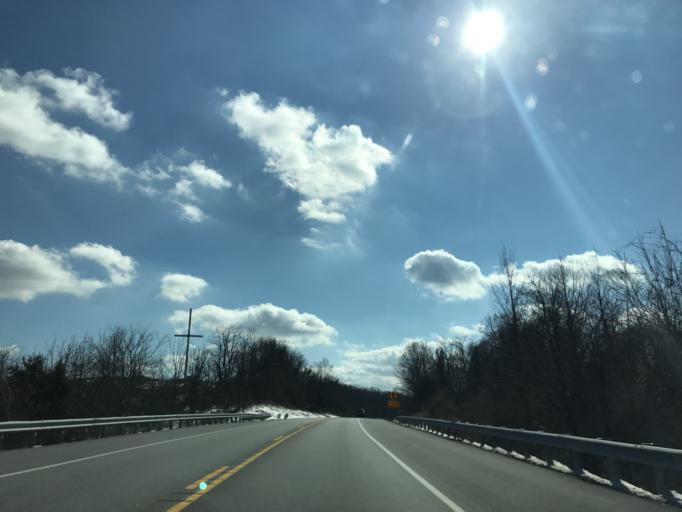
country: US
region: Maryland
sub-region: Carroll County
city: Westminster
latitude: 39.6030
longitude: -76.9447
